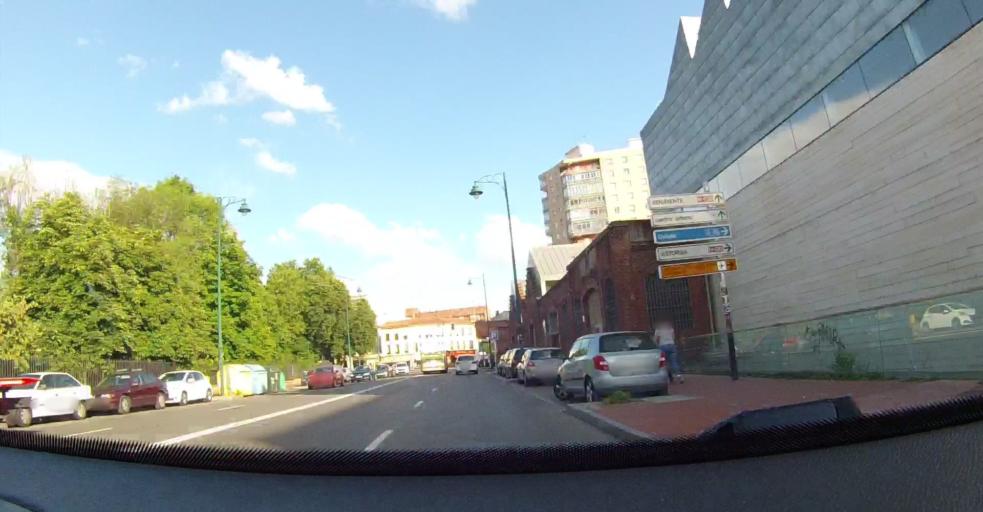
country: ES
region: Castille and Leon
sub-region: Provincia de Leon
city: Leon
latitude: 42.6010
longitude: -5.5868
